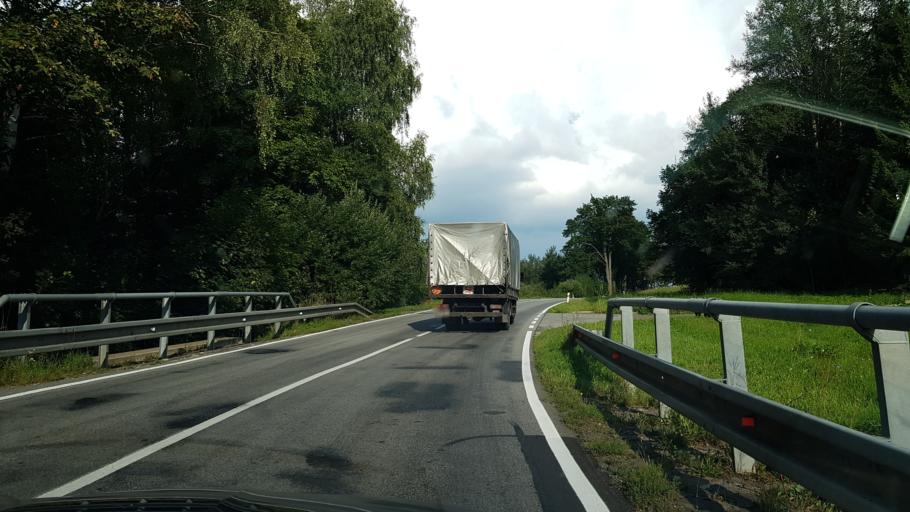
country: PL
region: Lower Silesian Voivodeship
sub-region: Powiat klodzki
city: Miedzylesie
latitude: 50.0995
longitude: 16.6323
